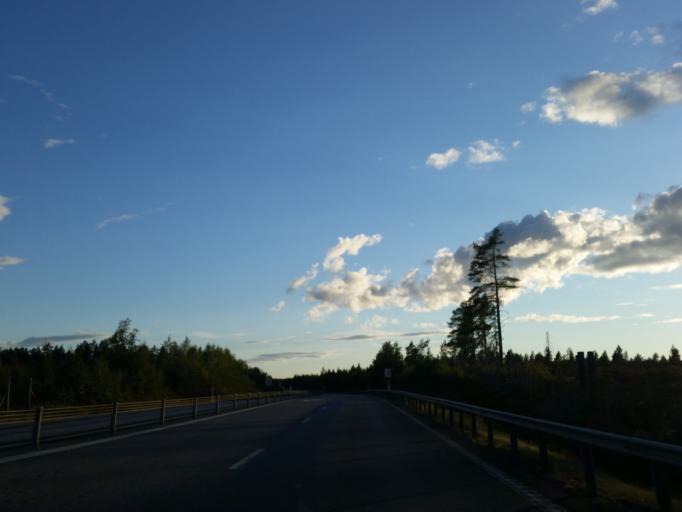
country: SE
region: Vaesterbotten
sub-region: Umea Kommun
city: Saevar
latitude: 63.9898
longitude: 20.7501
